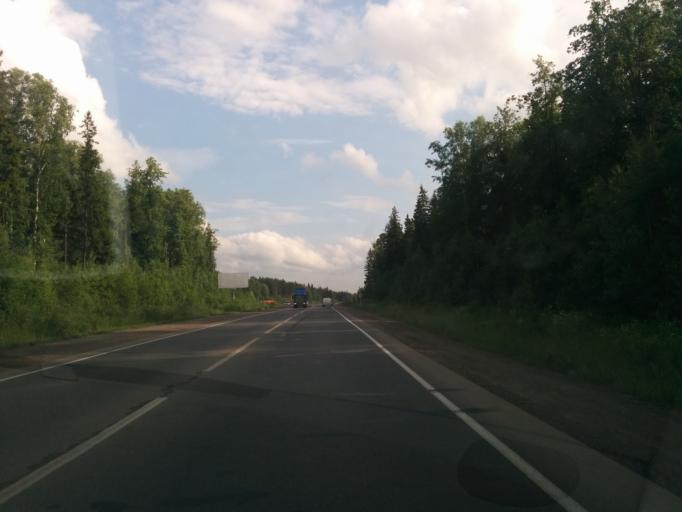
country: RU
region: Perm
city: Polazna
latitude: 58.1186
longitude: 56.4252
